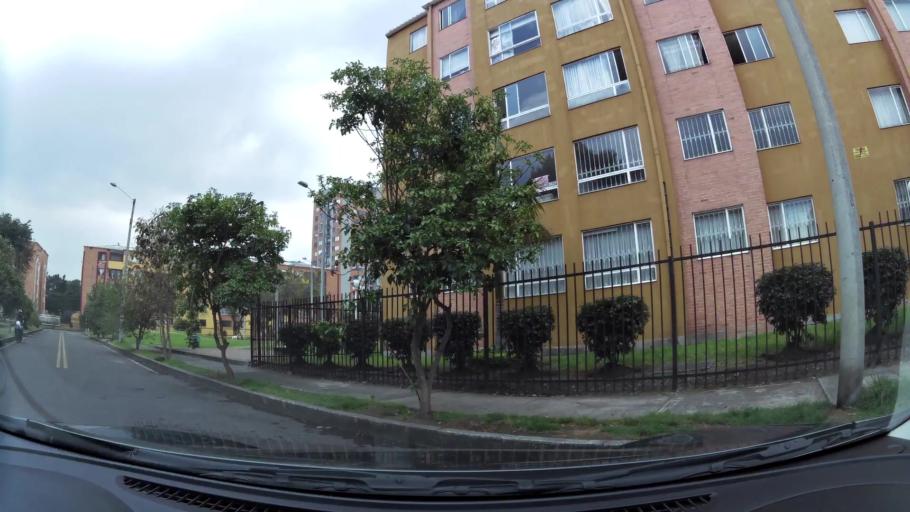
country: CO
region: Cundinamarca
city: Cota
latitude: 4.7476
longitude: -74.0523
